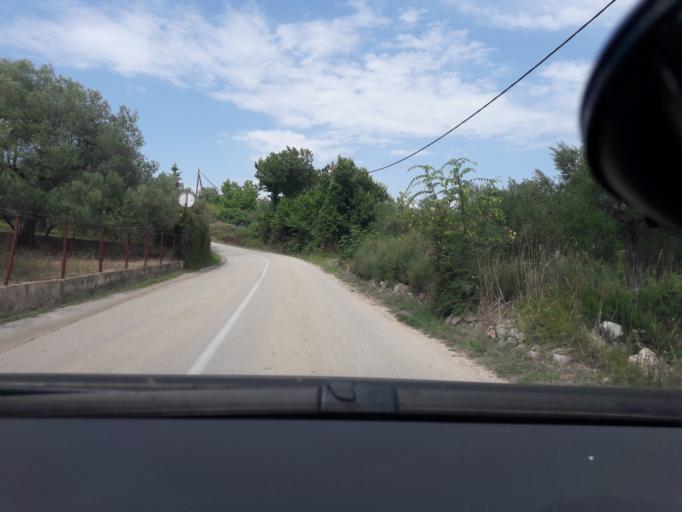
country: HR
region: Zadarska
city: Nin
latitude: 44.1671
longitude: 15.1880
